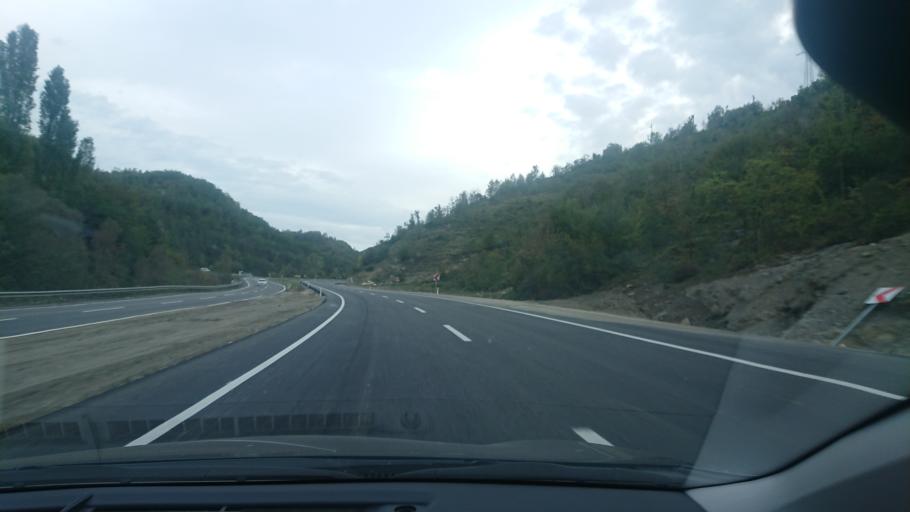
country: TR
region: Zonguldak
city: Beycuma
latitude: 41.3940
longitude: 31.9366
